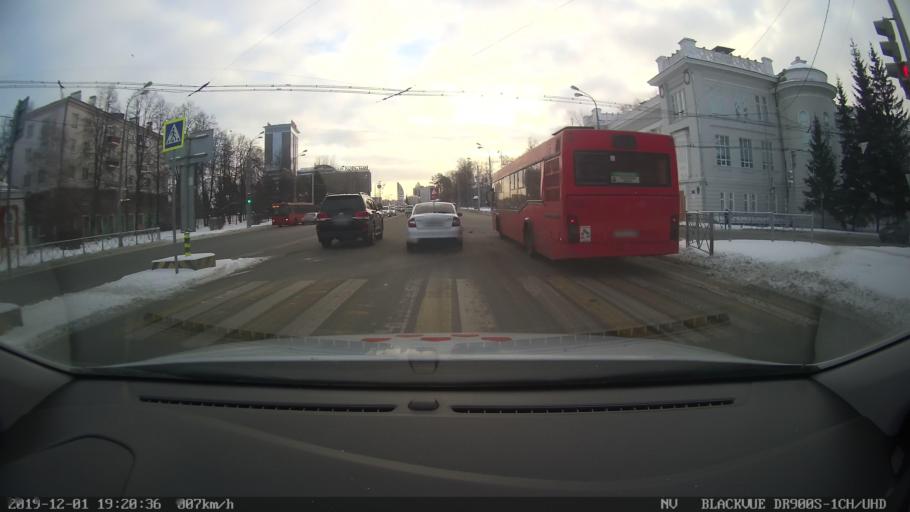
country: RU
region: Tatarstan
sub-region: Gorod Kazan'
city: Kazan
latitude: 55.7994
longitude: 49.1434
